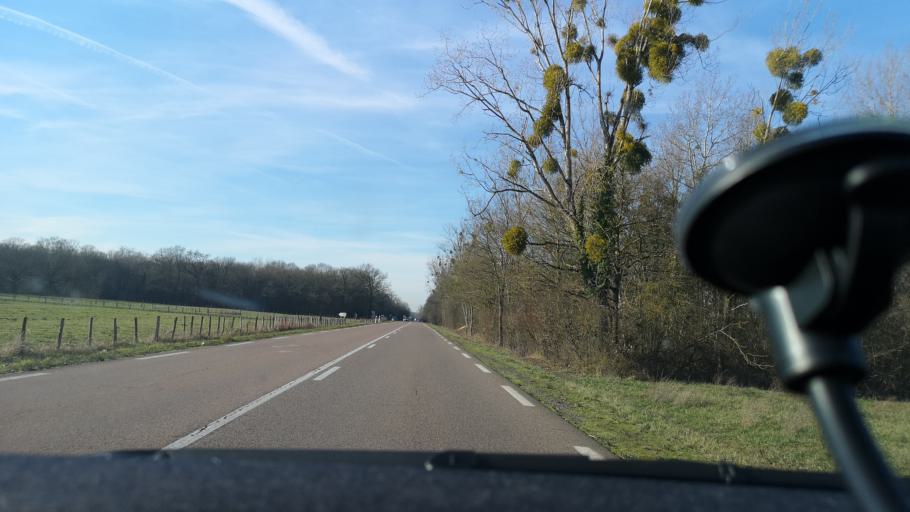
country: FR
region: Bourgogne
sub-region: Departement de la Cote-d'Or
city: Seurre
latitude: 46.9606
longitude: 5.1927
